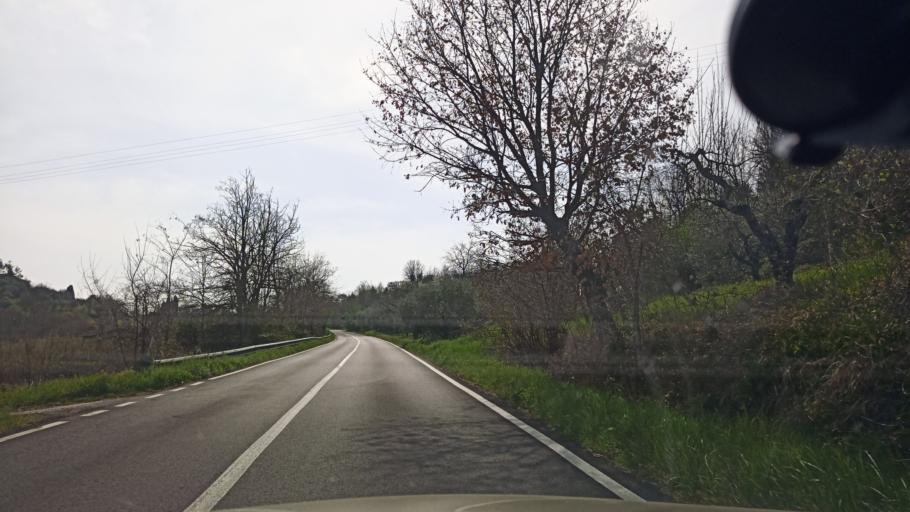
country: IT
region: Latium
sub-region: Provincia di Rieti
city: Cantalupo in Sabina
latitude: 42.3136
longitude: 12.6439
